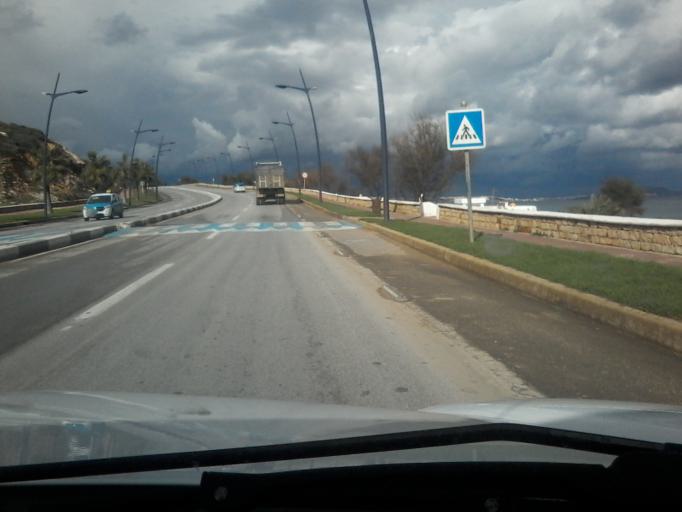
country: ES
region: Ceuta
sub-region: Ceuta
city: Ceuta
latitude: 35.7795
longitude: -5.3486
